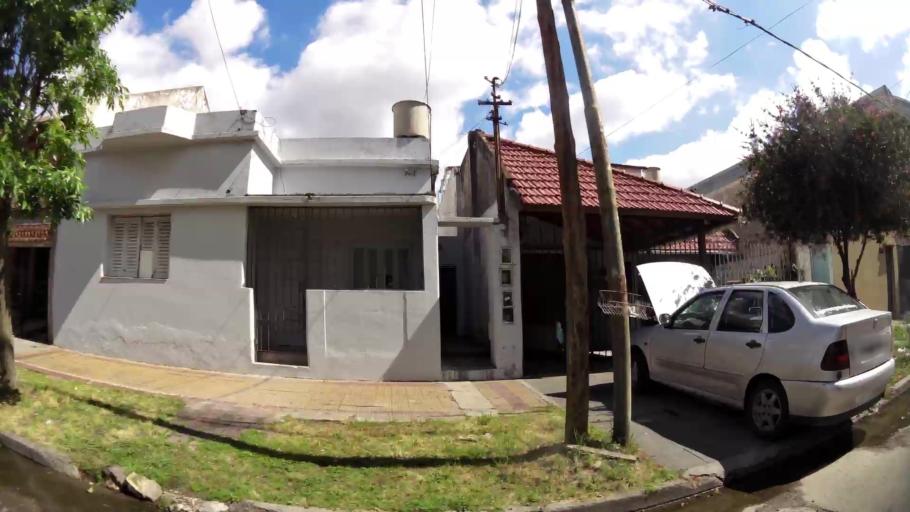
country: AR
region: Buenos Aires
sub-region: Partido de Lanus
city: Lanus
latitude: -34.6805
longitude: -58.4137
